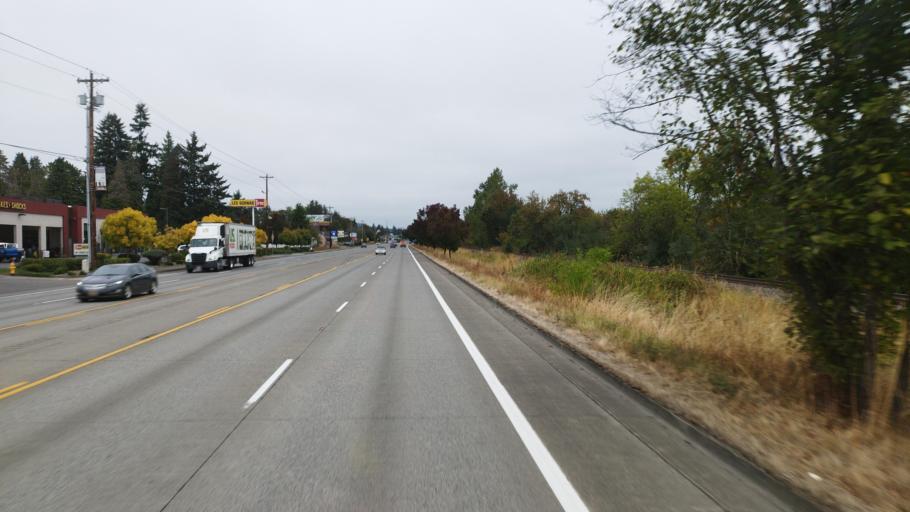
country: US
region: Oregon
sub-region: Columbia County
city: Warren
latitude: 45.8425
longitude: -122.8355
